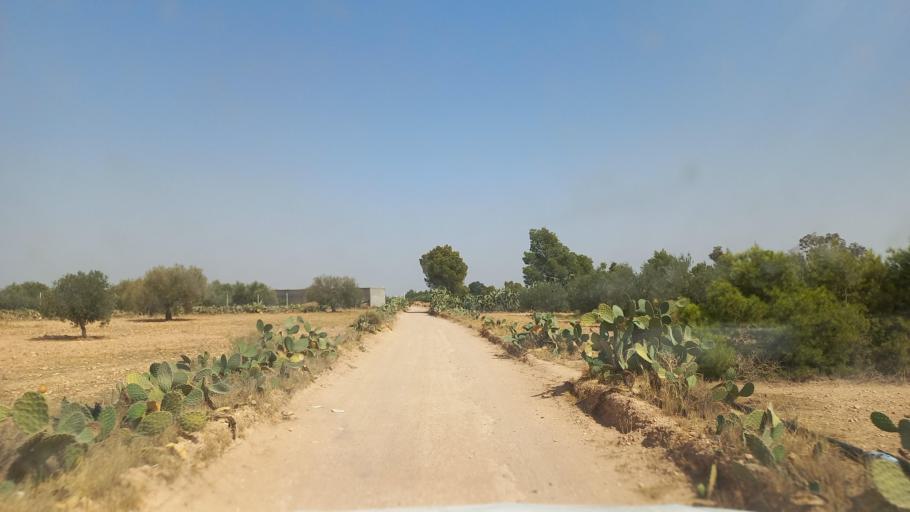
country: TN
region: Al Qasrayn
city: Kasserine
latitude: 35.2494
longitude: 9.0111
